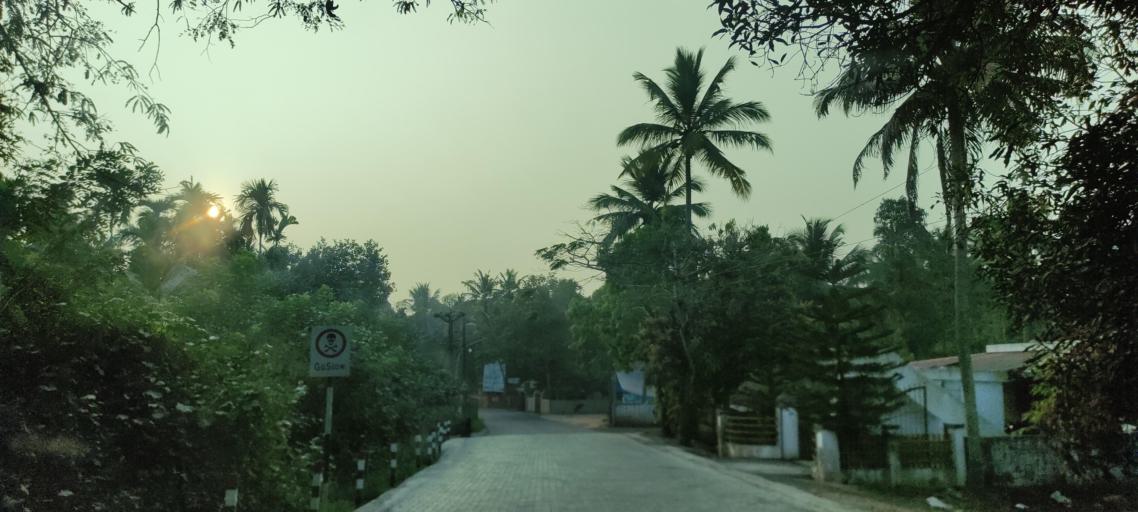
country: IN
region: Kerala
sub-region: Kottayam
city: Vaikam
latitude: 9.6878
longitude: 76.4268
